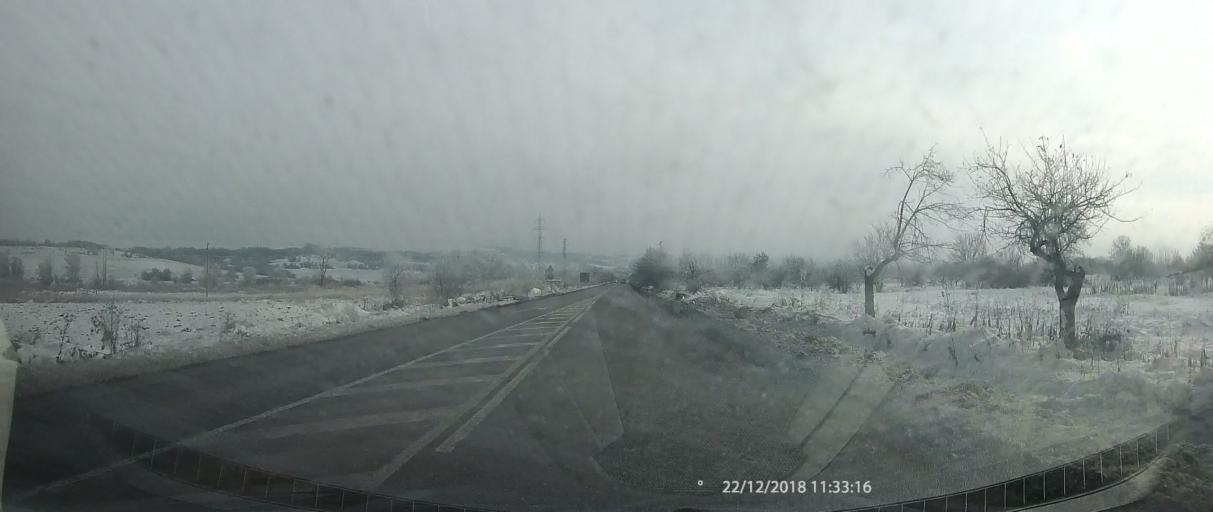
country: BG
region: Kyustendil
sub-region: Obshtina Dupnitsa
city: Dupnitsa
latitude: 42.2701
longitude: 23.0443
